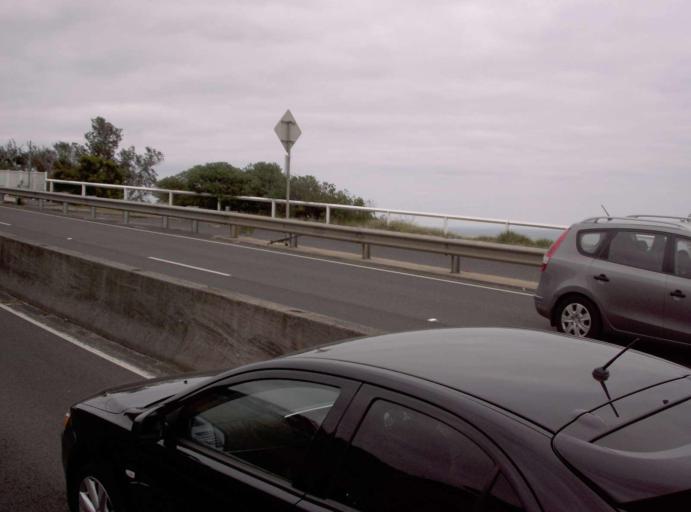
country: AU
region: Victoria
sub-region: Frankston
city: Frankston
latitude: -38.1550
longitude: 145.1068
